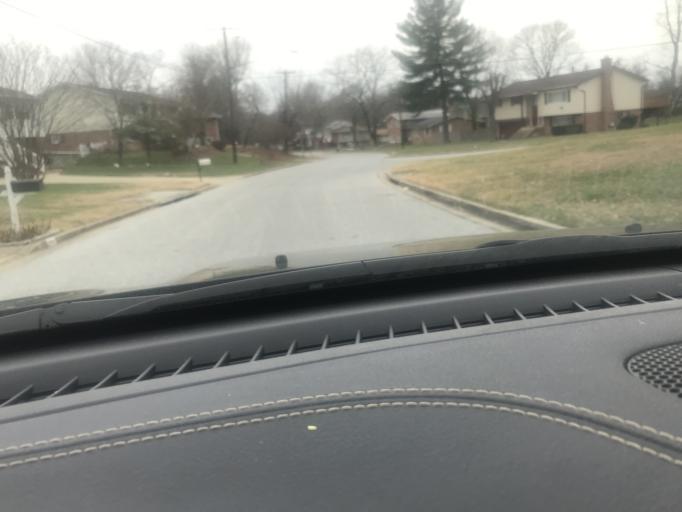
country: US
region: Maryland
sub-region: Prince George's County
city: Oxon Hill
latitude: 38.7958
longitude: -76.9698
